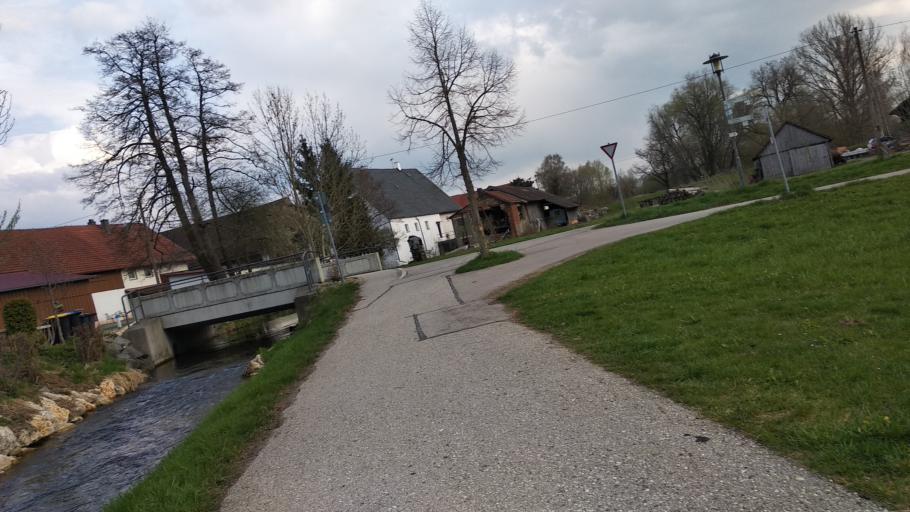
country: DE
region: Bavaria
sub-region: Swabia
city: Mindelheim
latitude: 48.0306
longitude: 10.4917
